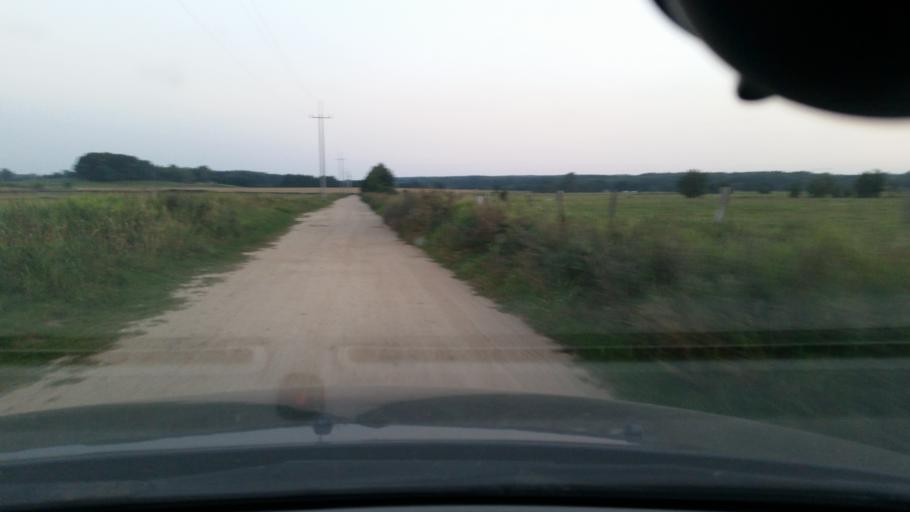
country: PL
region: Pomeranian Voivodeship
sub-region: Powiat wejherowski
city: Choczewo
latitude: 54.7794
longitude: 17.7926
